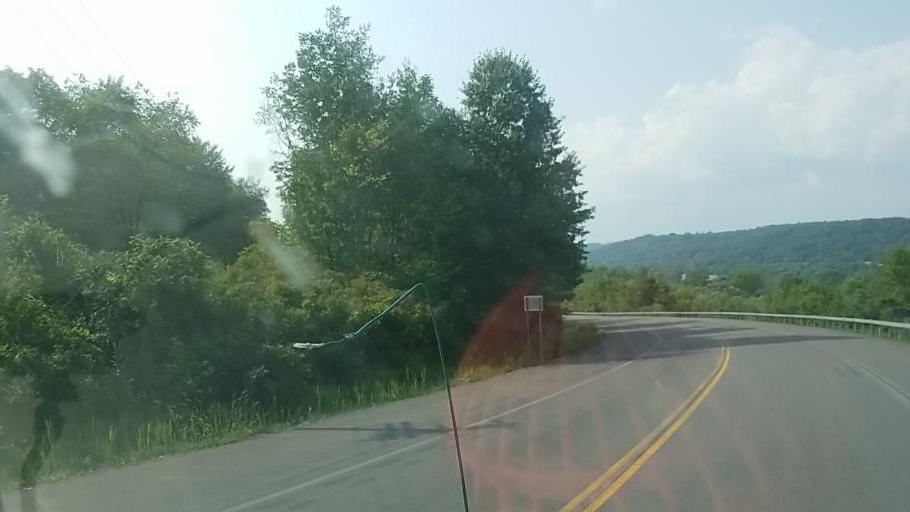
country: US
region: New York
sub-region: Montgomery County
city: Fonda
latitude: 42.9357
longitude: -74.3341
